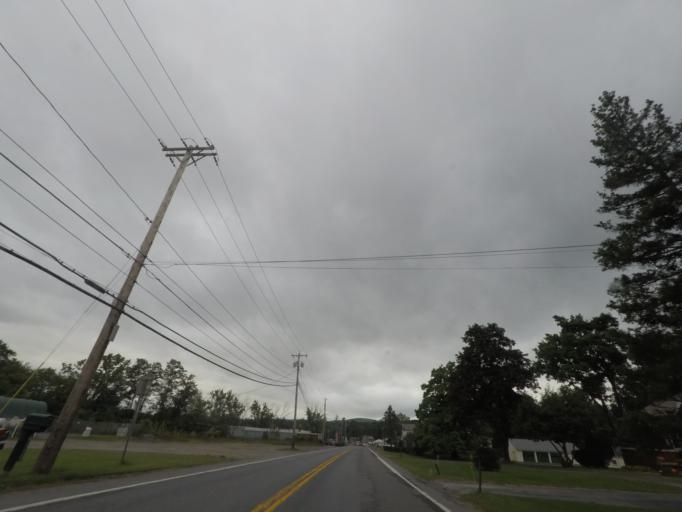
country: US
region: New York
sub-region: Rensselaer County
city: Hoosick Falls
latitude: 42.9177
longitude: -73.3504
